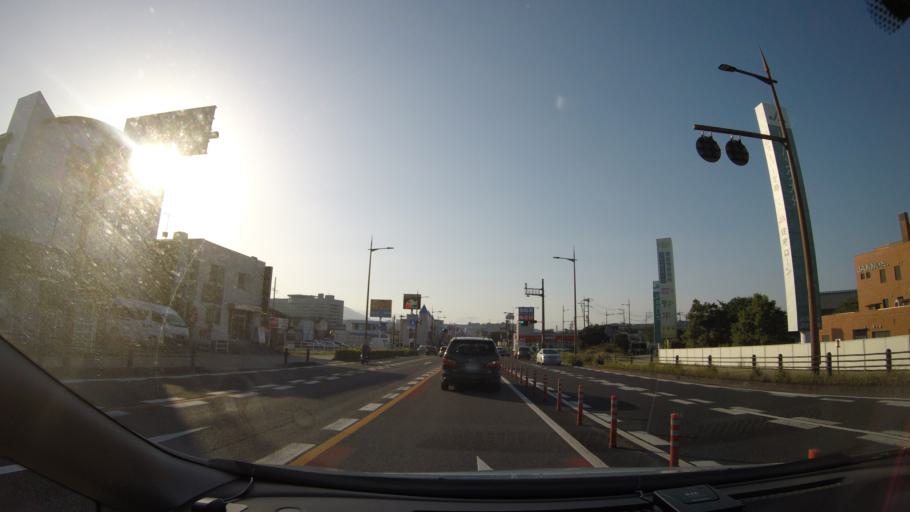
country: JP
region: Oita
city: Oita
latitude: 33.2046
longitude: 131.6037
